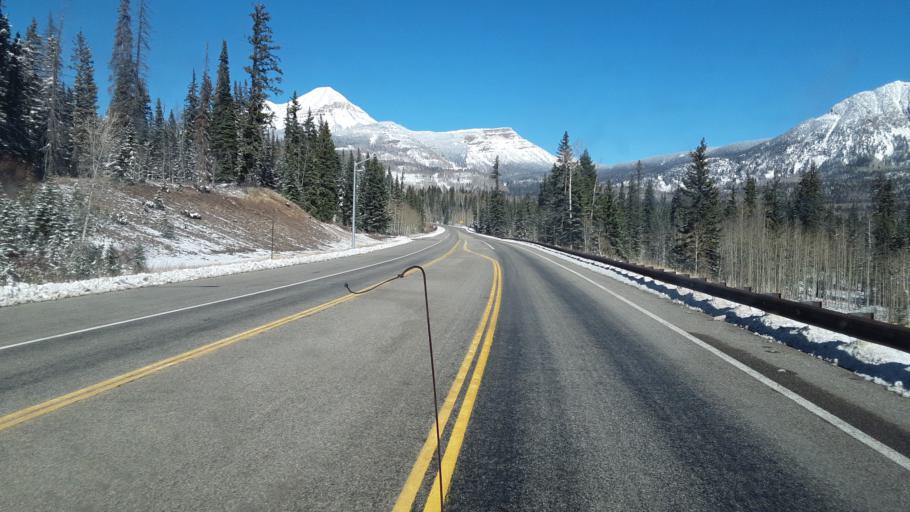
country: US
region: Colorado
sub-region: San Juan County
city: Silverton
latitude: 37.6351
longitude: -107.8072
